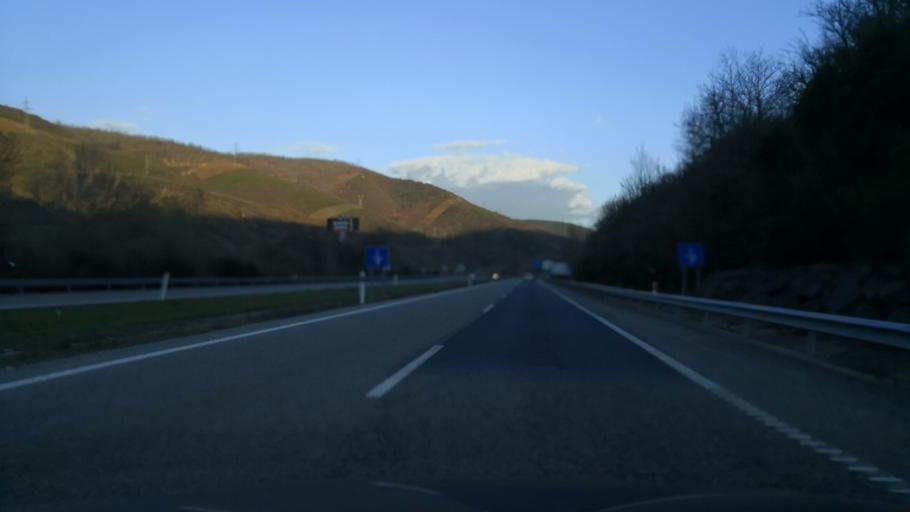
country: ES
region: Castille and Leon
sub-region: Provincia de Leon
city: Trabadelo
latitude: 42.6473
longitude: -6.8848
